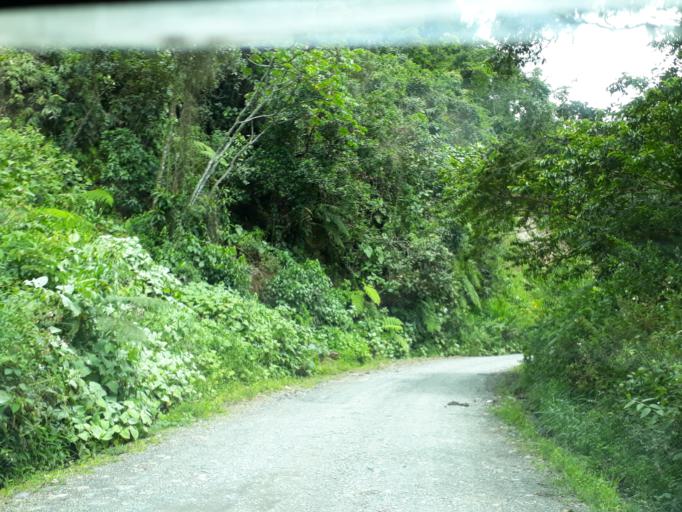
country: CO
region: Cundinamarca
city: Topaipi
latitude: 5.3372
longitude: -74.1870
